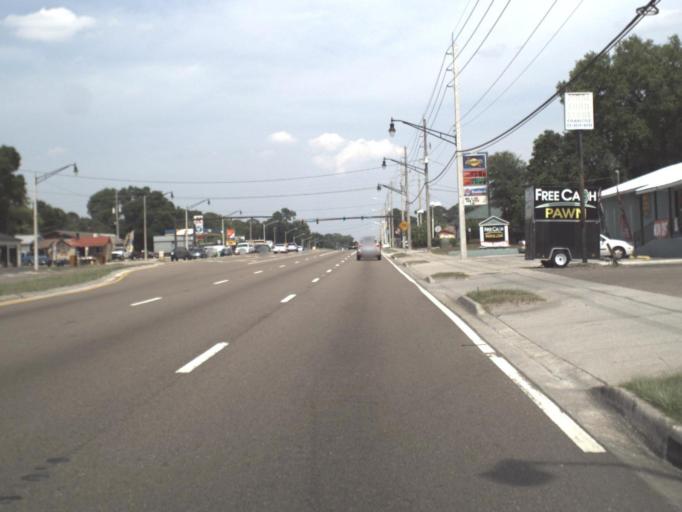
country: US
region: Florida
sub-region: Clay County
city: Bellair-Meadowbrook Terrace
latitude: 30.2479
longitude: -81.7876
